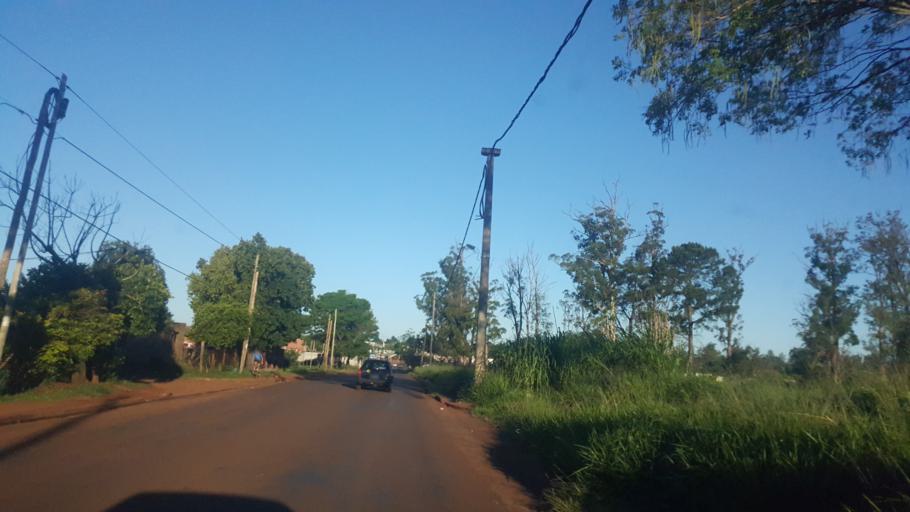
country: AR
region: Misiones
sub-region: Departamento de Capital
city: Posadas
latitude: -27.4246
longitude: -55.9460
